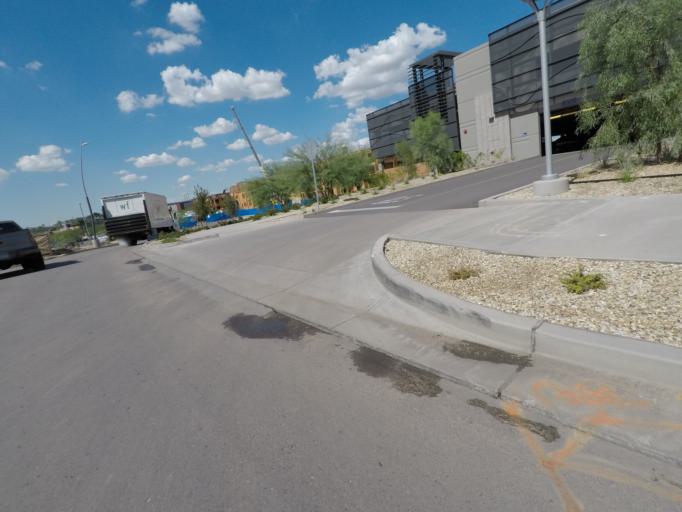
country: US
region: Arizona
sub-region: Maricopa County
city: Tempe
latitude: 33.4332
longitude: -111.8983
